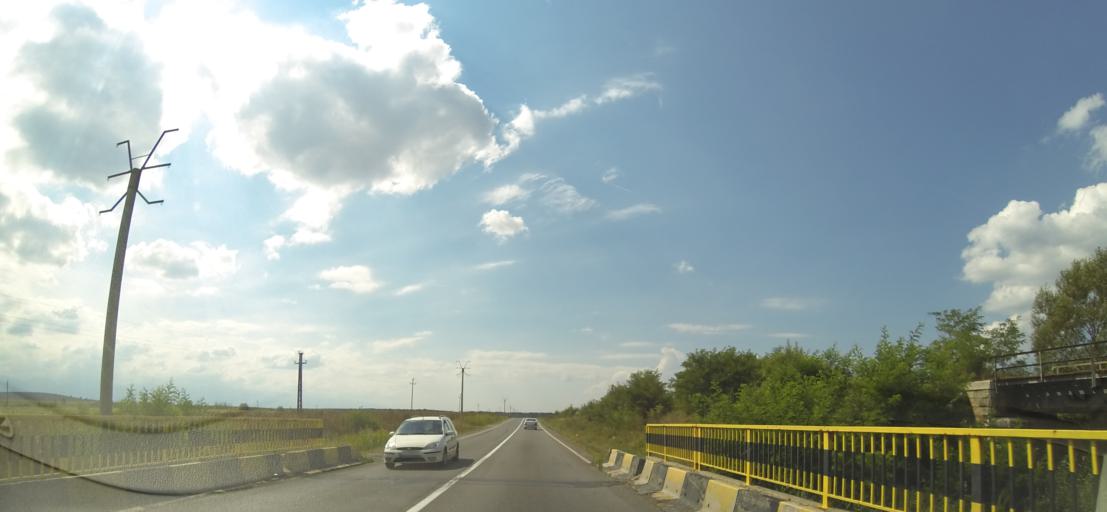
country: RO
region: Brasov
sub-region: Comuna Mandra
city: Mandra
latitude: 45.8237
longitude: 25.0864
